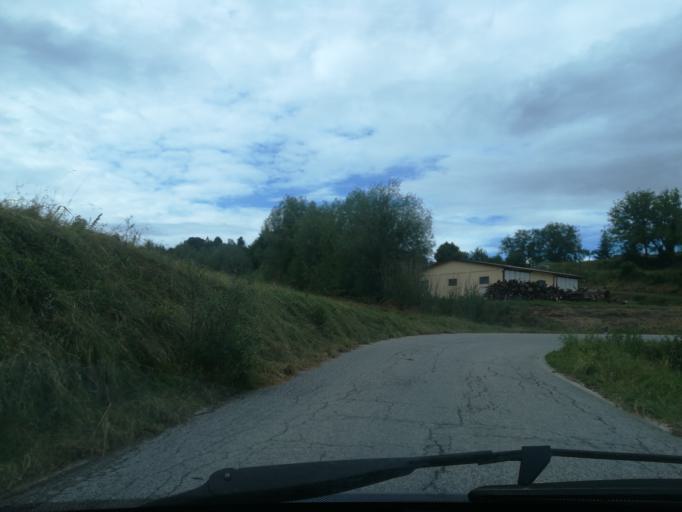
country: IT
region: The Marches
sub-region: Province of Fermo
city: Montefortino
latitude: 42.9353
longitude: 13.3733
